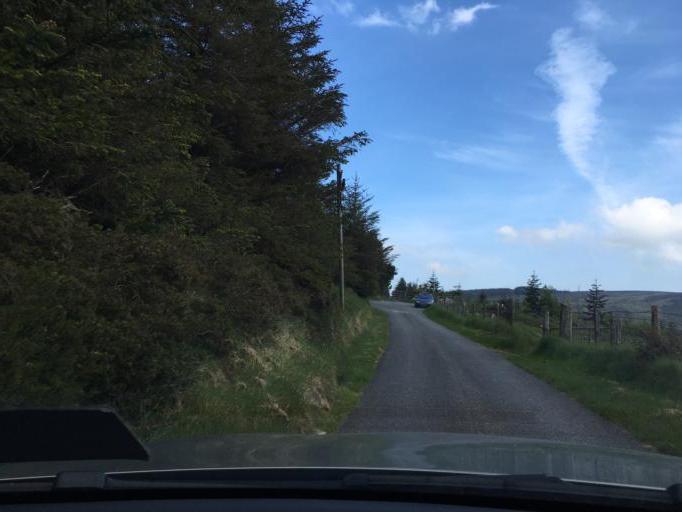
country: IE
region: Leinster
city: Ballinteer
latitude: 53.2482
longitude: -6.2709
